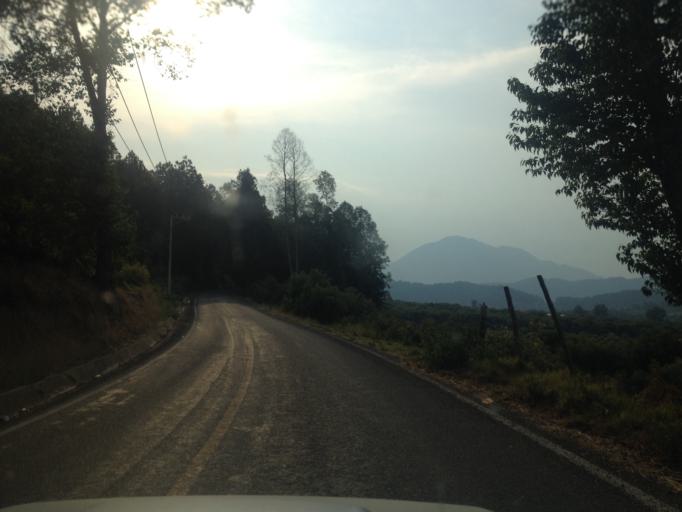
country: MX
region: Michoacan
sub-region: Zitacuaro
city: La Fundicion (Quinta Manzana)
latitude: 19.4881
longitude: -100.3198
